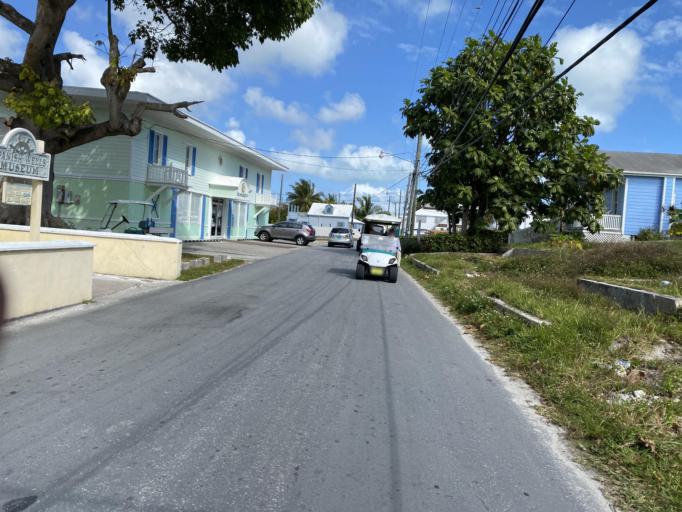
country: BS
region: Spanish Wells
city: Spanish Wells
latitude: 25.5437
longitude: -76.7505
